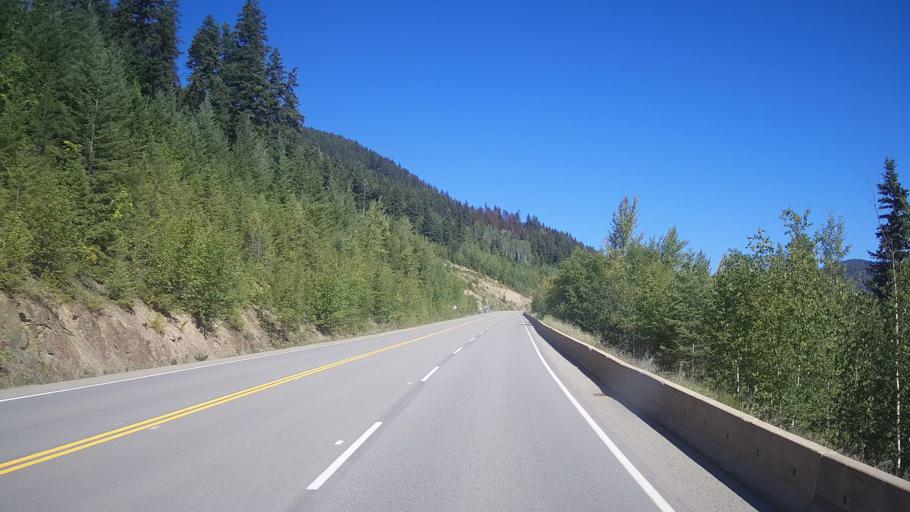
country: CA
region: British Columbia
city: Kamloops
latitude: 51.4682
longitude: -120.2527
